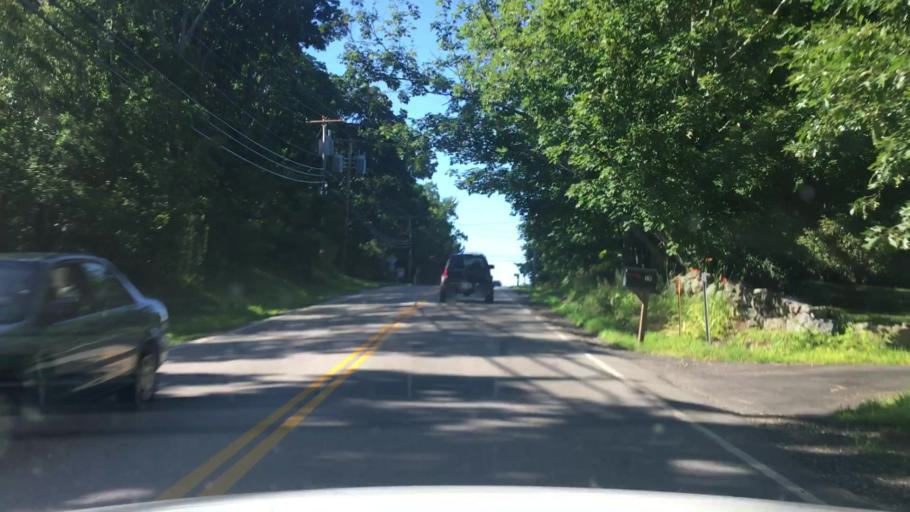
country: US
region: New Hampshire
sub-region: Rockingham County
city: Exeter
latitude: 42.9985
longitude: -70.9468
